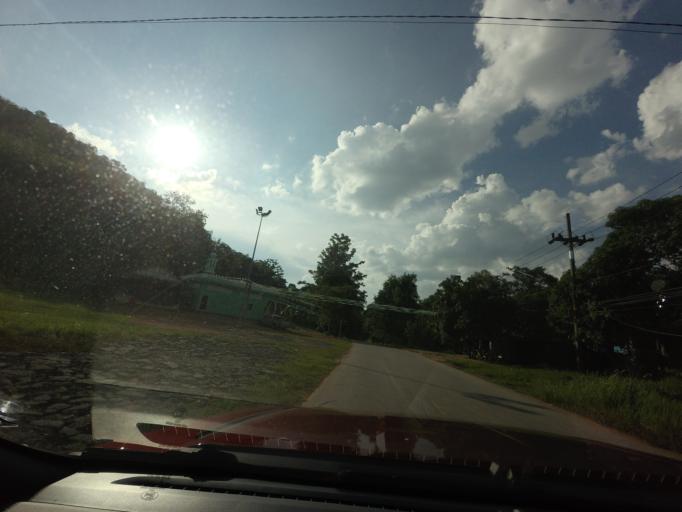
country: TH
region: Yala
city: Ban Nang Sata
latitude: 6.2108
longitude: 101.2340
